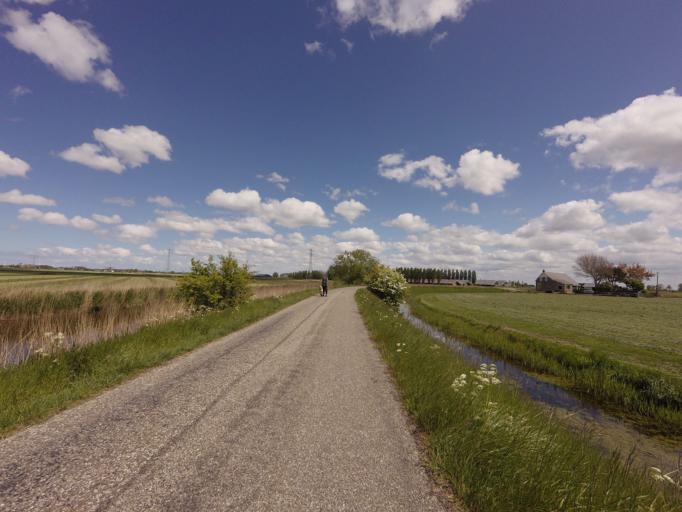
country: NL
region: Friesland
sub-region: Gemeente Franekeradeel
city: Franeker
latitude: 53.1473
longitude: 5.4954
